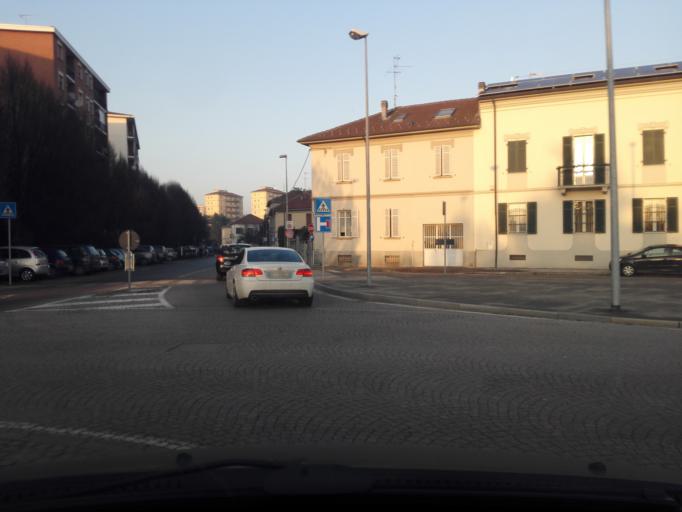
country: IT
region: Piedmont
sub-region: Provincia di Alessandria
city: Alessandria
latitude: 44.9010
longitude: 8.6076
